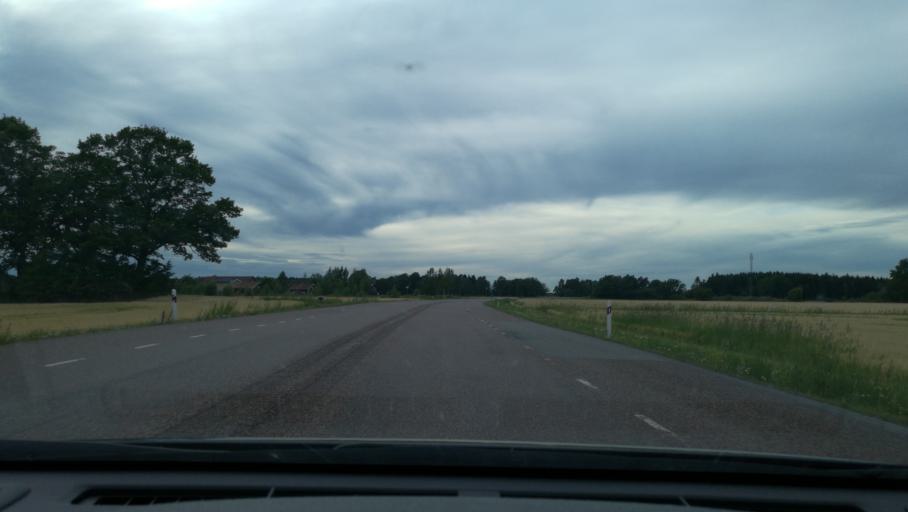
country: SE
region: Vaestmanland
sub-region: Kopings Kommun
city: Koping
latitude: 59.4612
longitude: 16.0013
